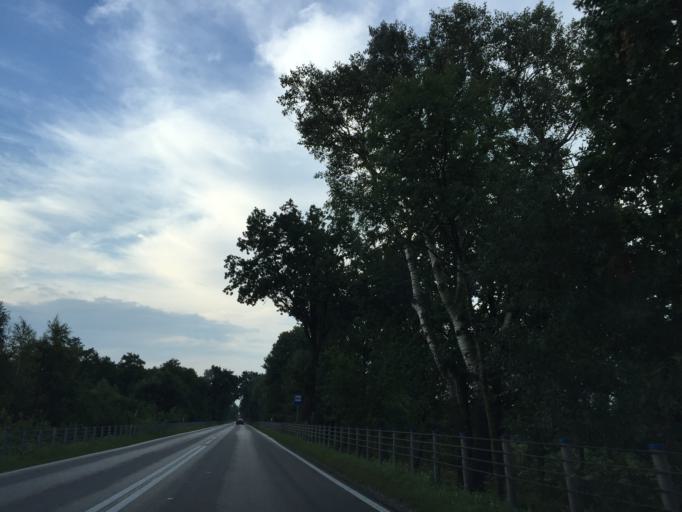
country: PL
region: Masovian Voivodeship
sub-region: Powiat wegrowski
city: Sadowne
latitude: 52.6654
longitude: 21.8489
